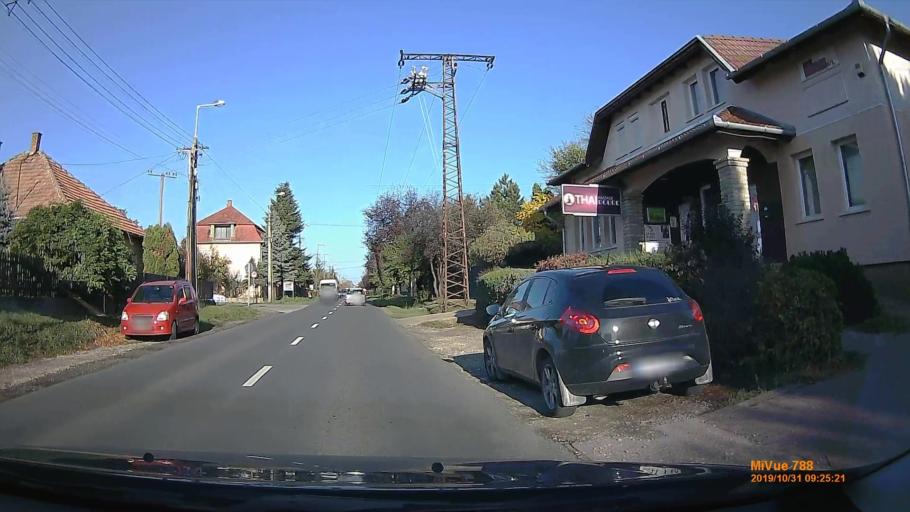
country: HU
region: Pest
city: Maglod
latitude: 47.4416
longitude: 19.3715
